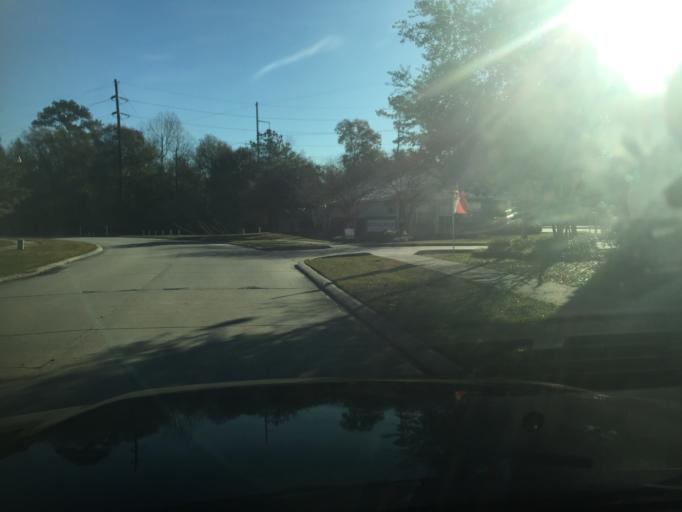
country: US
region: Louisiana
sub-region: Saint Tammany Parish
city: Slidell
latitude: 30.2482
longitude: -89.7678
